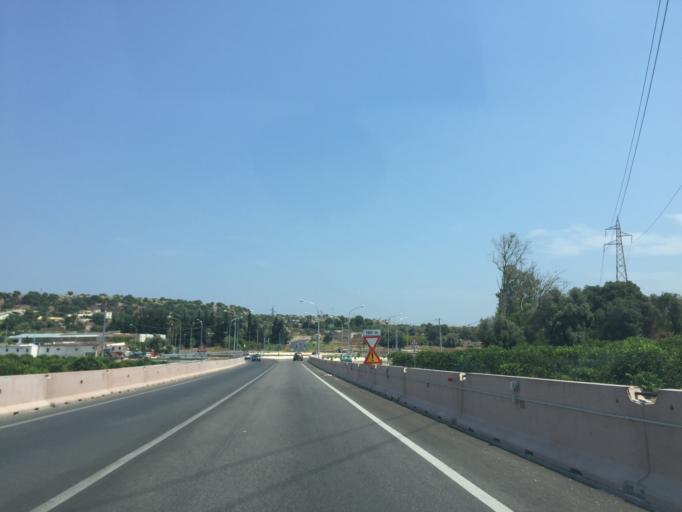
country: IT
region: Sicily
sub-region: Provincia di Siracusa
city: Siracusa
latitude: 37.0745
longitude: 15.2470
